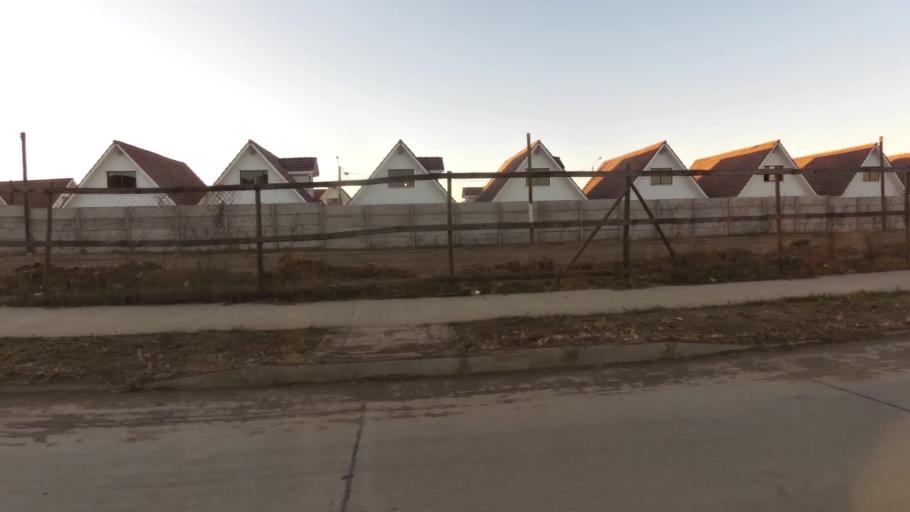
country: CL
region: O'Higgins
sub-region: Provincia de Cachapoal
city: Rancagua
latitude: -34.1922
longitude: -70.7404
